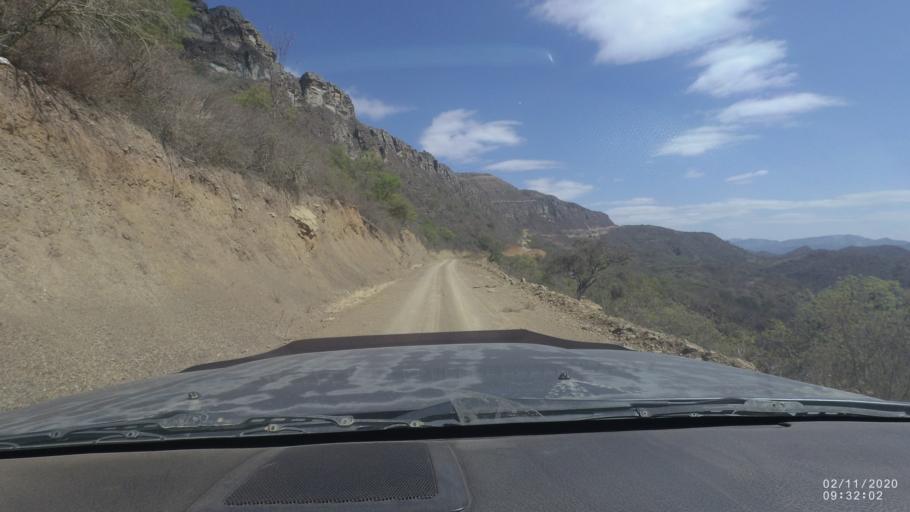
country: BO
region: Chuquisaca
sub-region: Provincia Zudanez
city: Mojocoya
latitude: -18.4234
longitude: -64.5854
